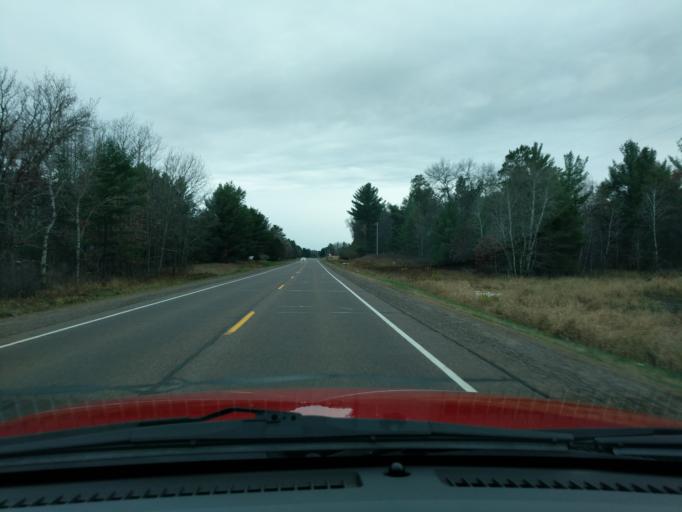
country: US
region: Wisconsin
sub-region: Washburn County
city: Spooner
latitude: 45.8218
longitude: -91.9141
